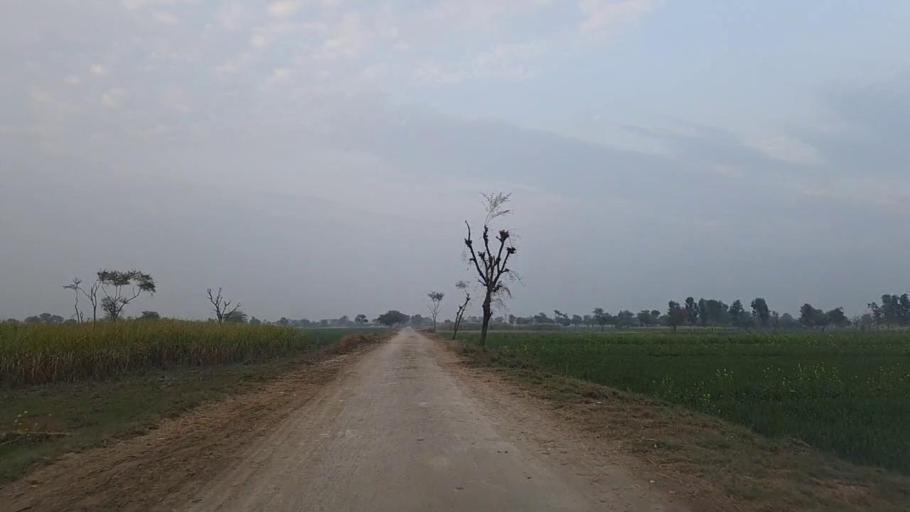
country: PK
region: Sindh
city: Jam Sahib
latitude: 26.2934
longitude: 68.5934
